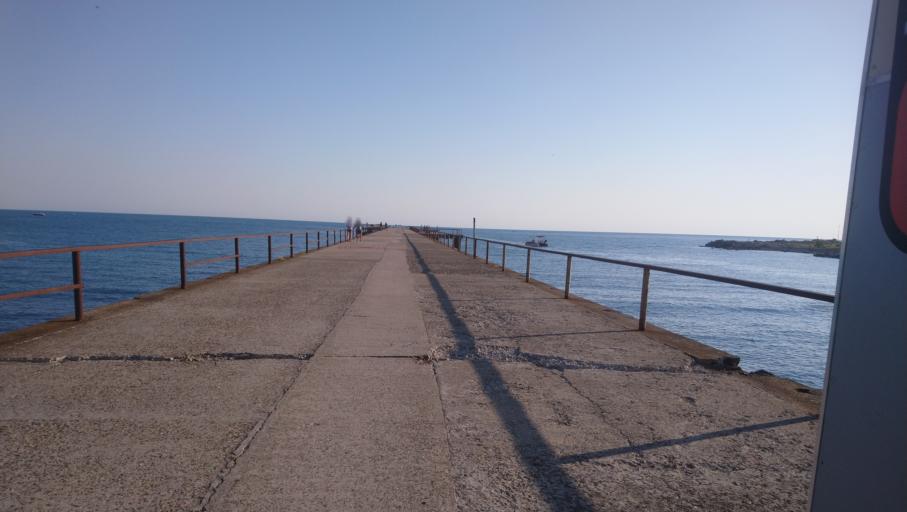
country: RU
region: Krasnodarskiy
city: Lermontovo
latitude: 44.3015
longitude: 38.7455
